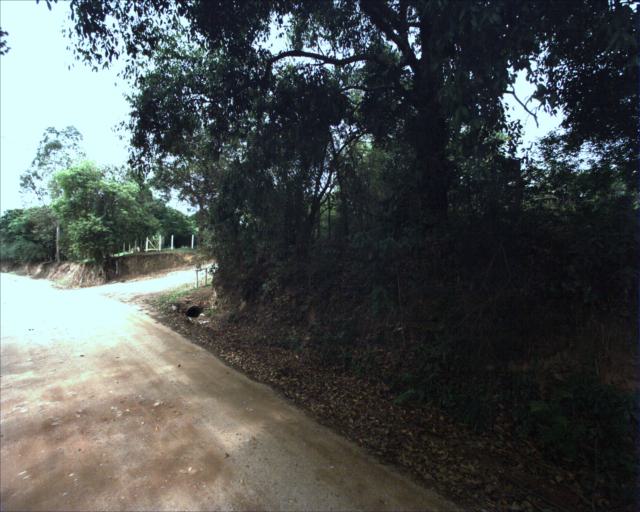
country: BR
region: Sao Paulo
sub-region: Sorocaba
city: Sorocaba
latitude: -23.4657
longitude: -47.3949
